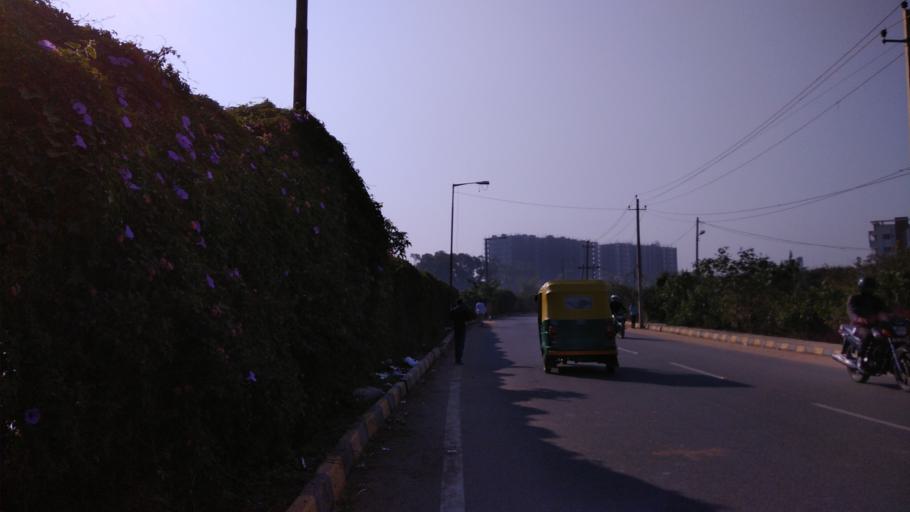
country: IN
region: Karnataka
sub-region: Bangalore Rural
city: Hoskote
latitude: 12.9744
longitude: 77.7340
